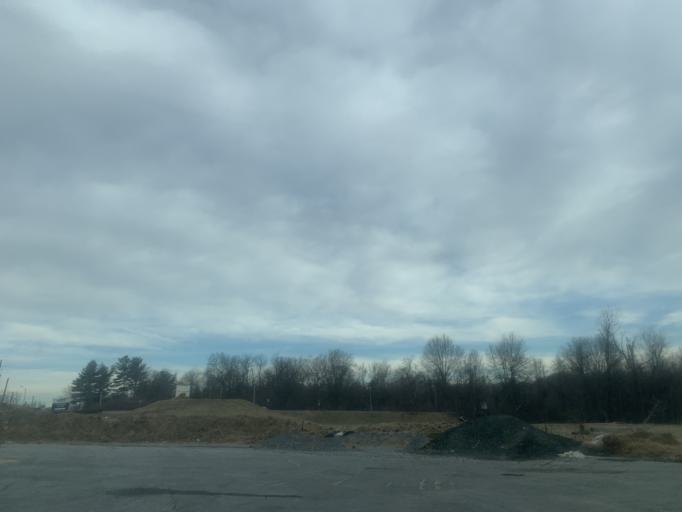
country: US
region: Maryland
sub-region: Prince George's County
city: Forestville
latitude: 38.8286
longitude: -76.8549
